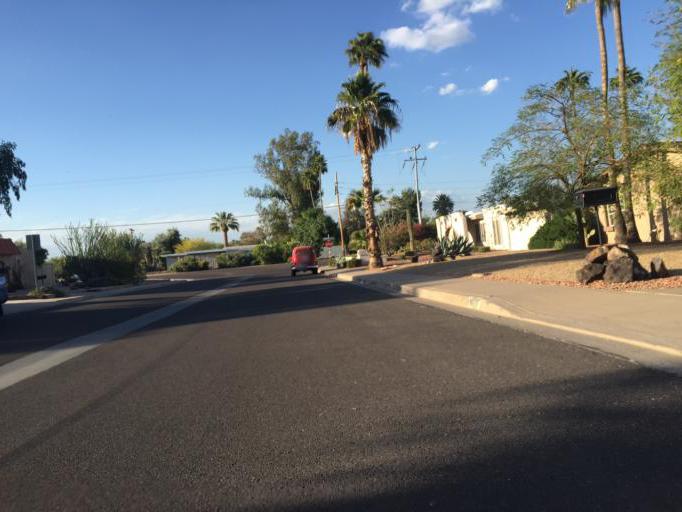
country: US
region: Arizona
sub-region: Maricopa County
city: Paradise Valley
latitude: 33.5747
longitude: -112.0052
